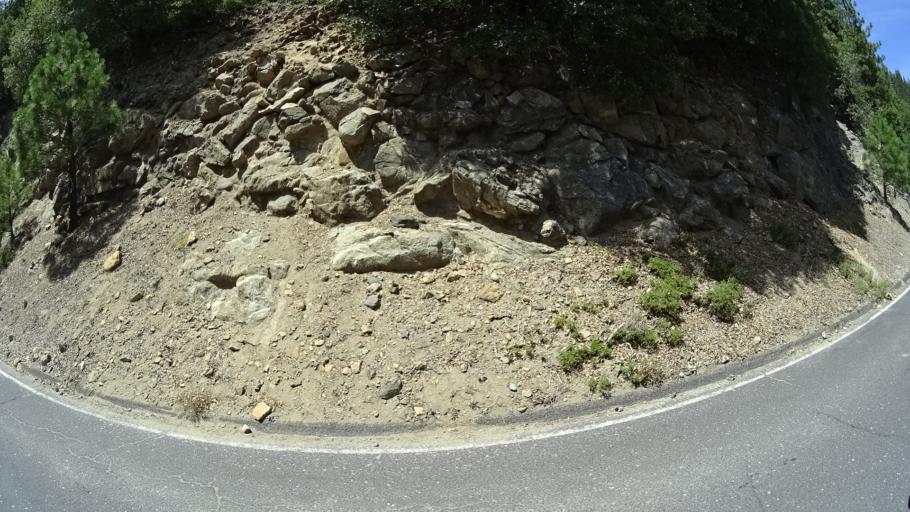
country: US
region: California
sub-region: Calaveras County
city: Arnold
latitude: 38.3160
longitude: -120.2301
